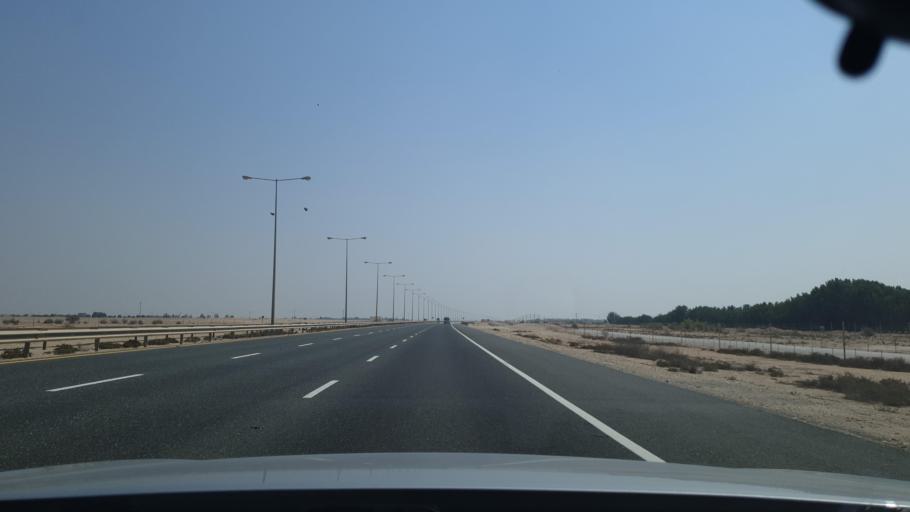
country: QA
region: Al Khawr
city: Al Khawr
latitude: 25.7798
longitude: 51.4039
